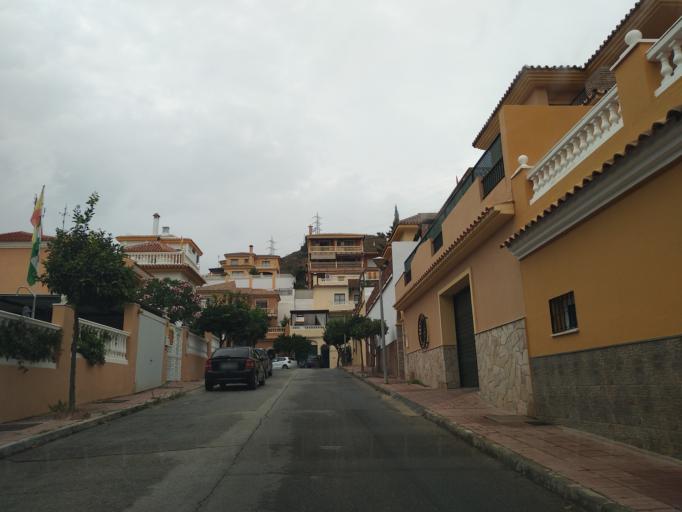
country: ES
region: Andalusia
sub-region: Provincia de Malaga
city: Malaga
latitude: 36.7433
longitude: -4.4755
